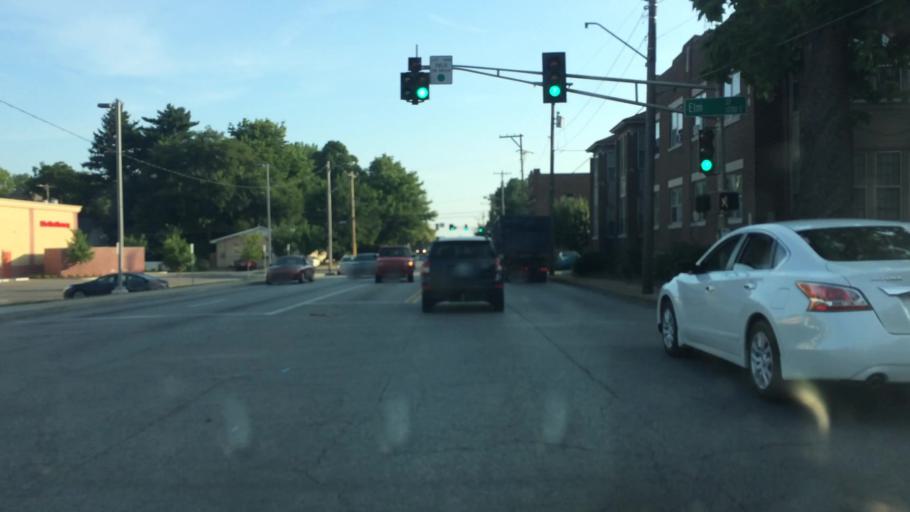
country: US
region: Missouri
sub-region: Greene County
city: Springfield
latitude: 37.2050
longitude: -93.2761
